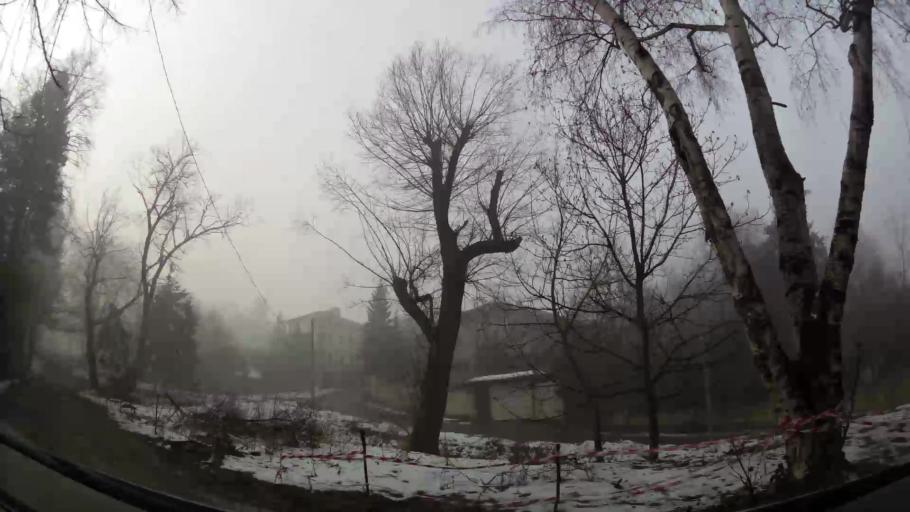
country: BG
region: Sofia-Capital
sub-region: Stolichna Obshtina
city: Sofia
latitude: 42.6582
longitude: 23.2492
